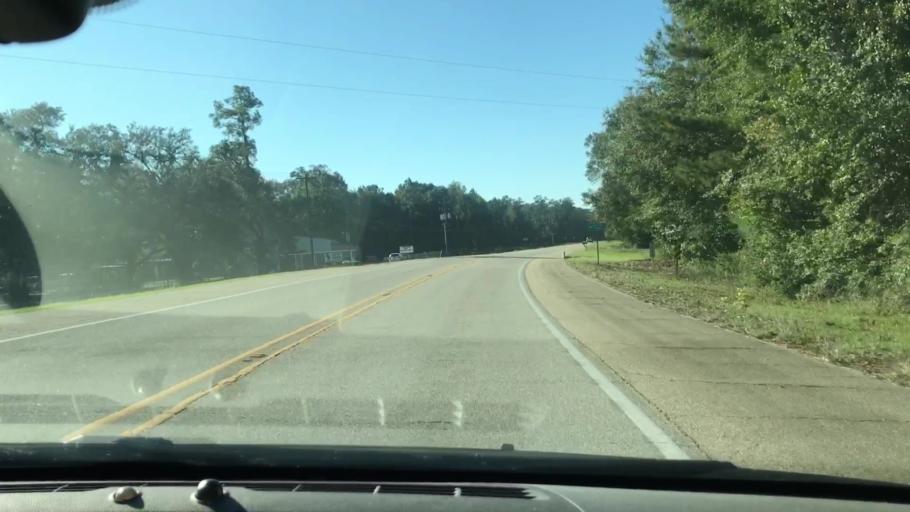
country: US
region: Mississippi
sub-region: Pearl River County
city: Nicholson
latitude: 30.4820
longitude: -89.8093
